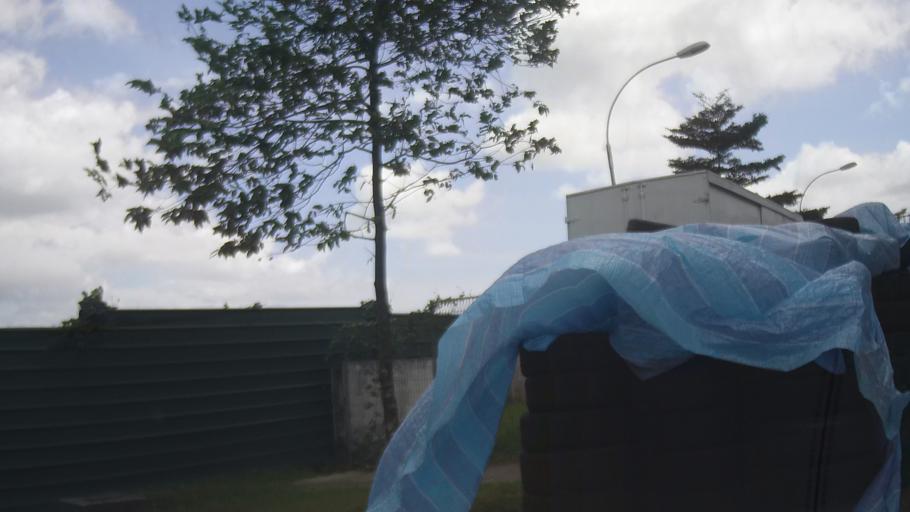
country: MY
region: Johor
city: Johor Bahru
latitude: 1.4087
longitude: 103.7590
